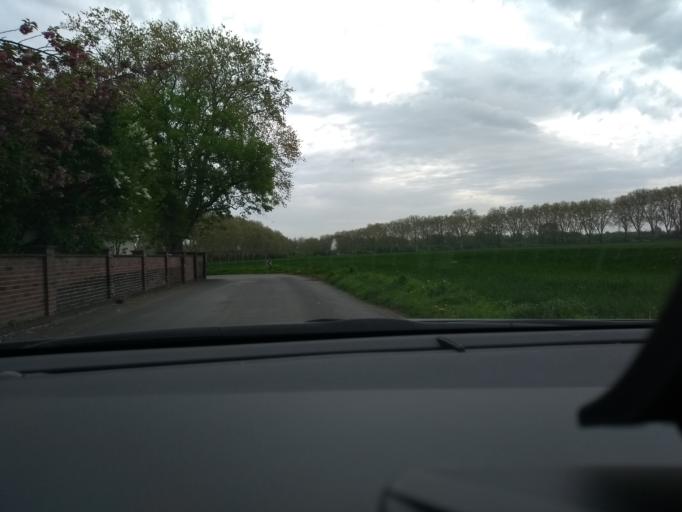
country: DE
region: North Rhine-Westphalia
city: Lunen
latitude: 51.6010
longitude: 7.5160
